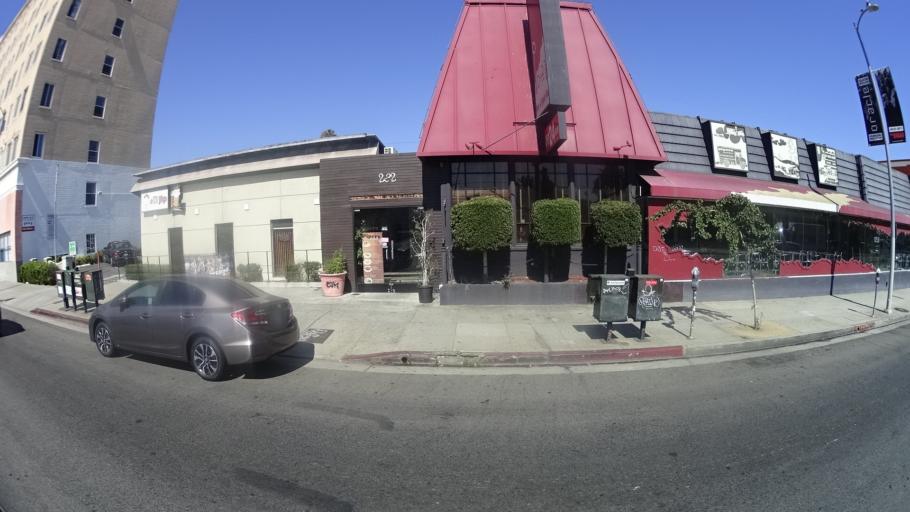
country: US
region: California
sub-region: Los Angeles County
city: Hollywood
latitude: 34.0756
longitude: -118.3091
